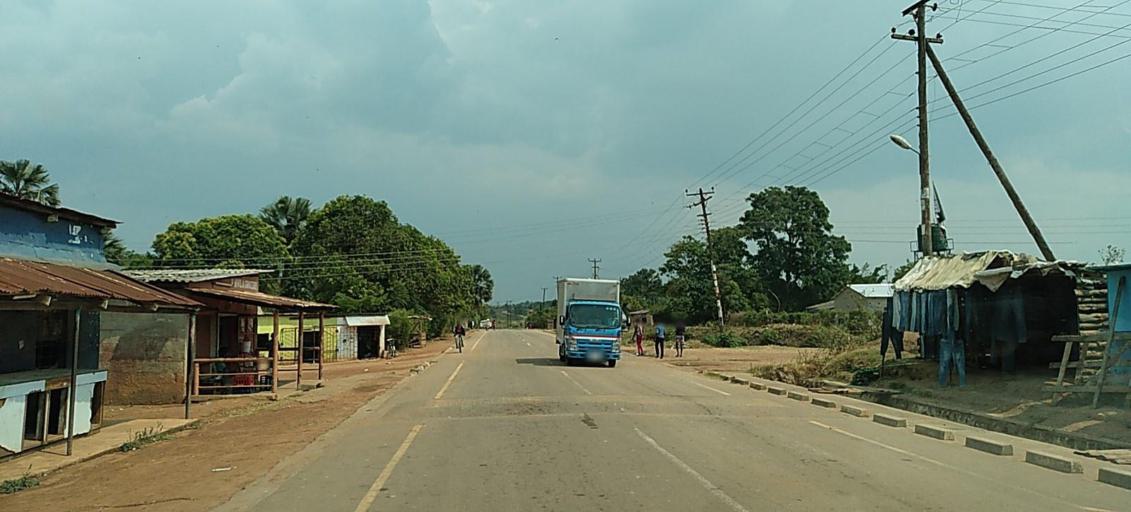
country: ZM
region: Copperbelt
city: Kalulushi
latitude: -12.8520
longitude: 28.1376
